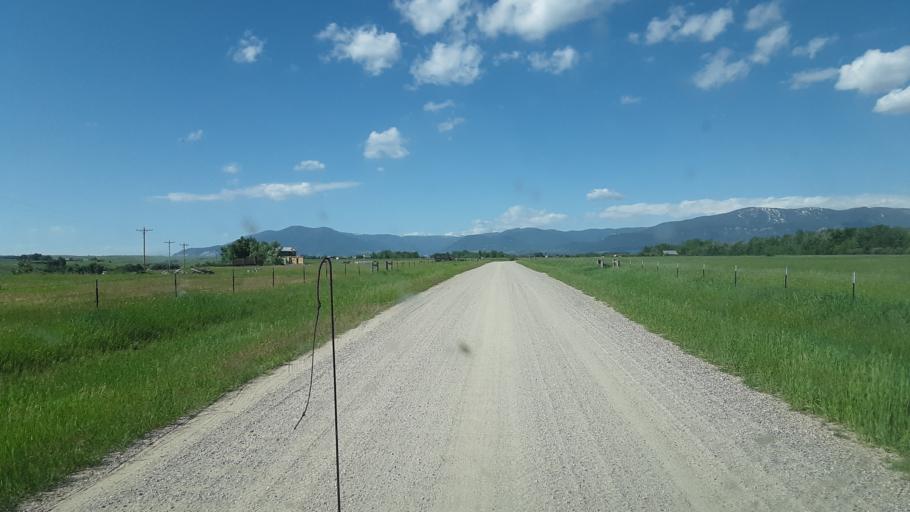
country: US
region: Montana
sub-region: Carbon County
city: Red Lodge
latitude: 45.2806
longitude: -109.1917
